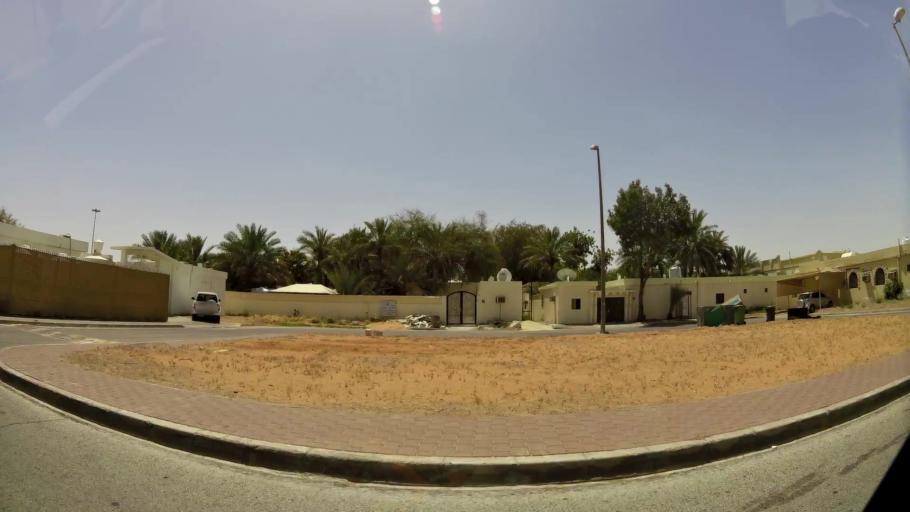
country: OM
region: Al Buraimi
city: Al Buraymi
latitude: 24.2827
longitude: 55.7644
